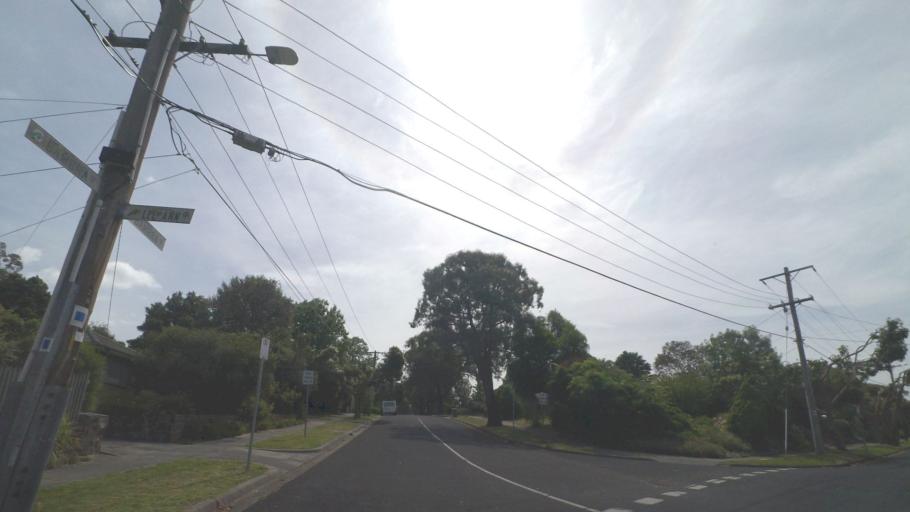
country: AU
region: Victoria
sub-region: Maroondah
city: Croydon North
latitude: -37.7783
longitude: 145.3024
